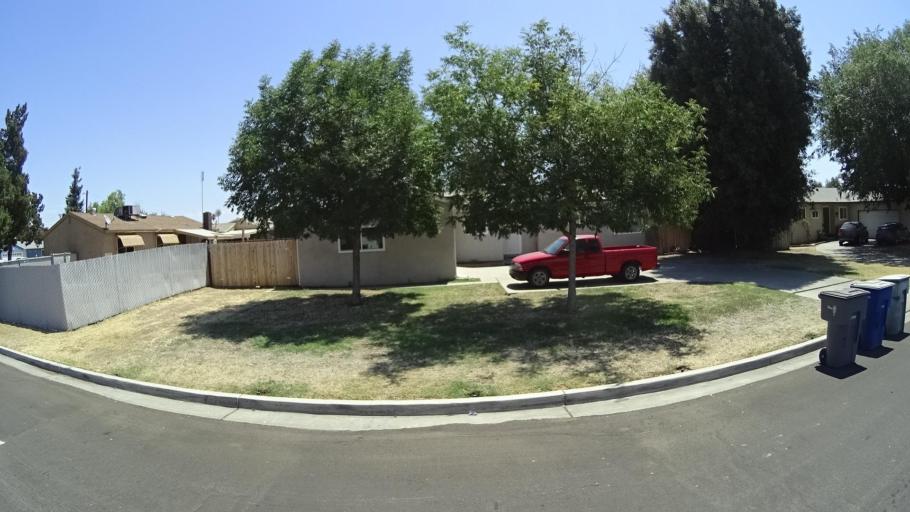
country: US
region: California
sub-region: Fresno County
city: Sunnyside
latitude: 36.7597
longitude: -119.7263
